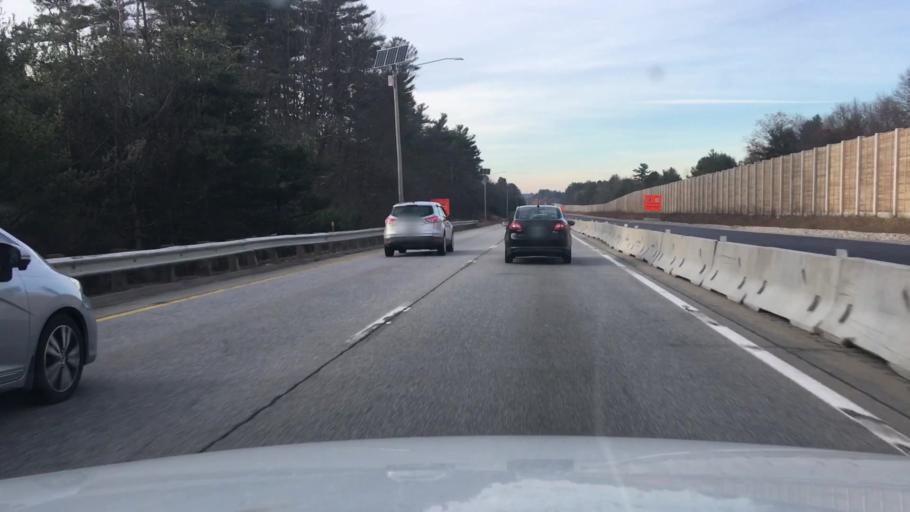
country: US
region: New Hampshire
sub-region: Rockingham County
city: Auburn
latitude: 42.9443
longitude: -71.3896
